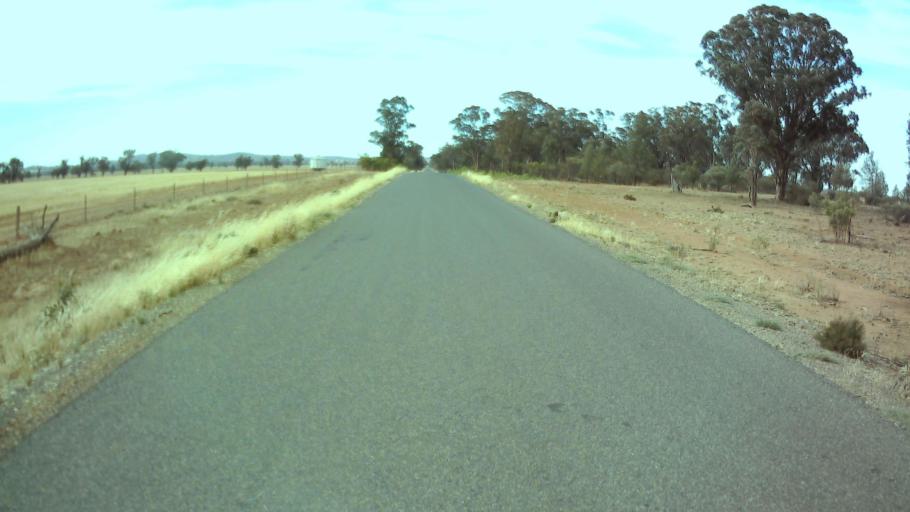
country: AU
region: New South Wales
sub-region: Weddin
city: Grenfell
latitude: -33.8861
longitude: 147.8551
